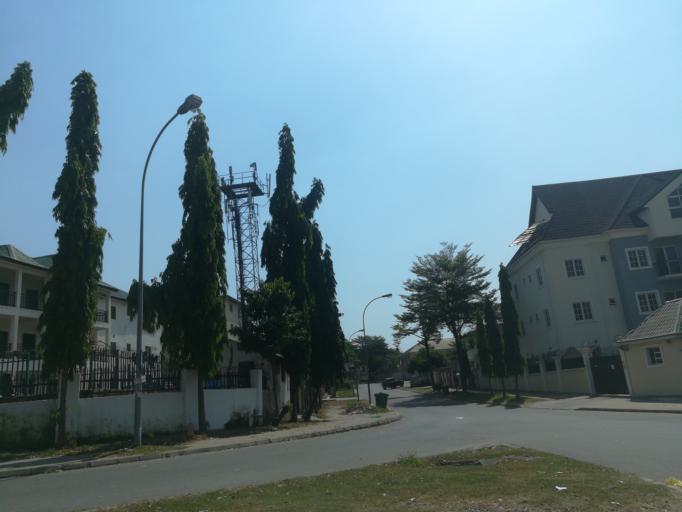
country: NG
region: Abuja Federal Capital Territory
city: Abuja
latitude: 9.0740
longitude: 7.4462
